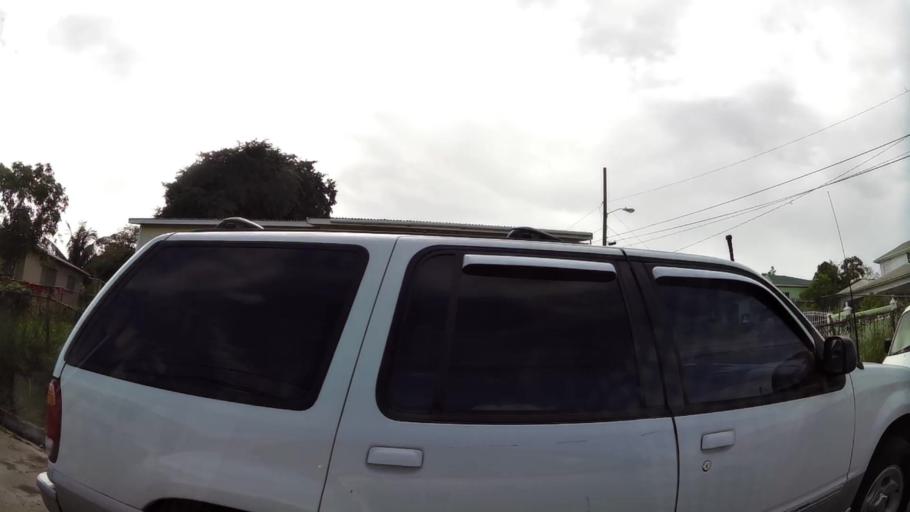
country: AG
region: Saint George
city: Piggotts
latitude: 17.1094
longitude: -61.8136
